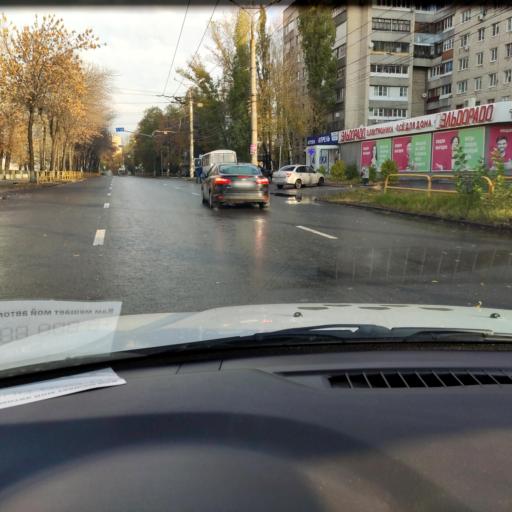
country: RU
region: Samara
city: Tol'yatti
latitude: 53.5091
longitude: 49.4224
